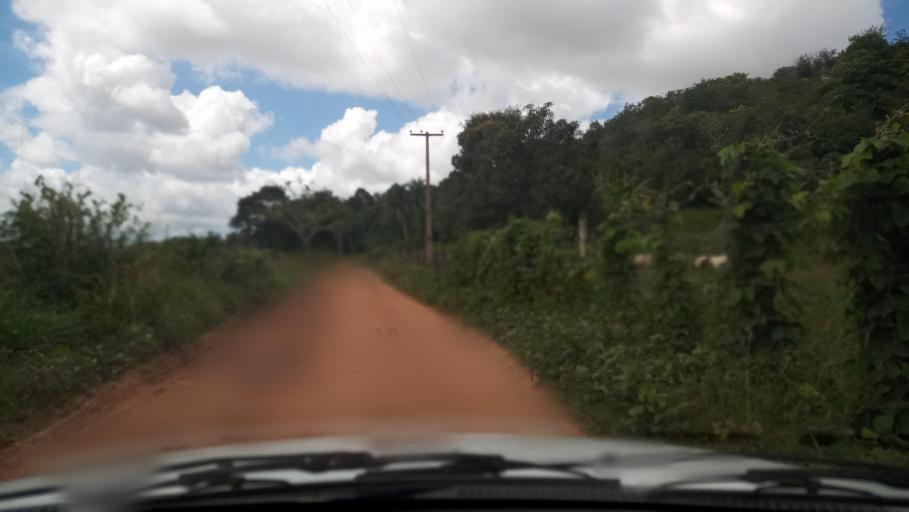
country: BR
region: Rio Grande do Norte
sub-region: Goianinha
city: Goianinha
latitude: -6.2605
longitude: -35.2497
